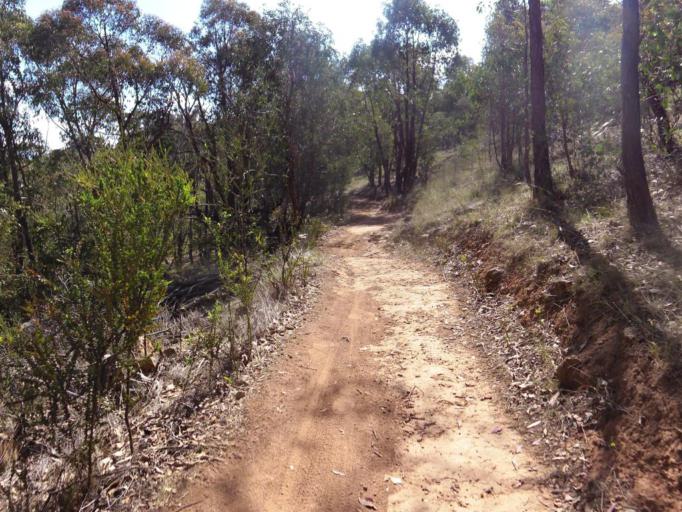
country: AU
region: Australian Capital Territory
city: Belconnen
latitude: -35.1552
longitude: 149.0833
